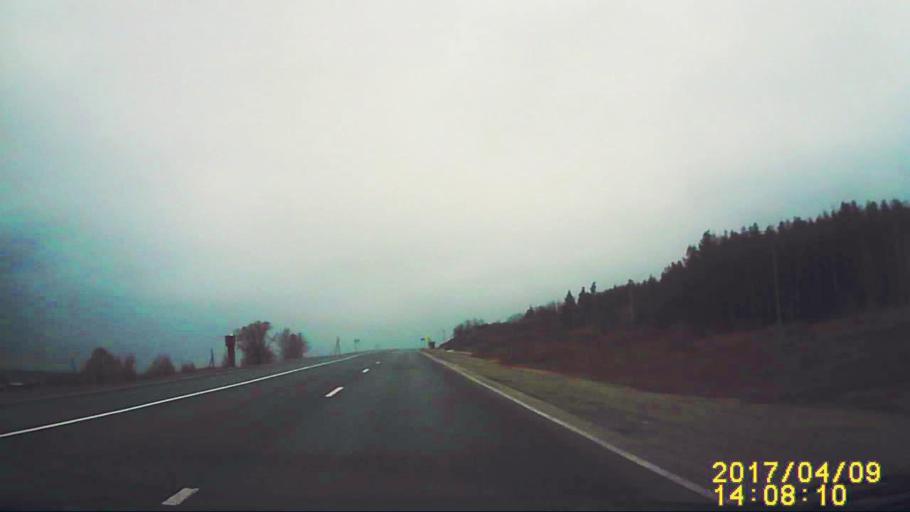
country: RU
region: Ulyanovsk
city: Silikatnyy
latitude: 54.0180
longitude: 48.2162
